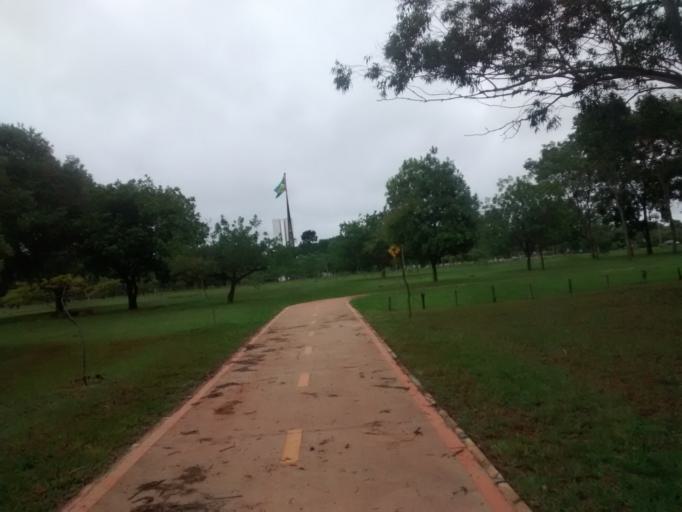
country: BR
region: Federal District
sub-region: Brasilia
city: Brasilia
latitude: -15.8026
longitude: -47.8547
